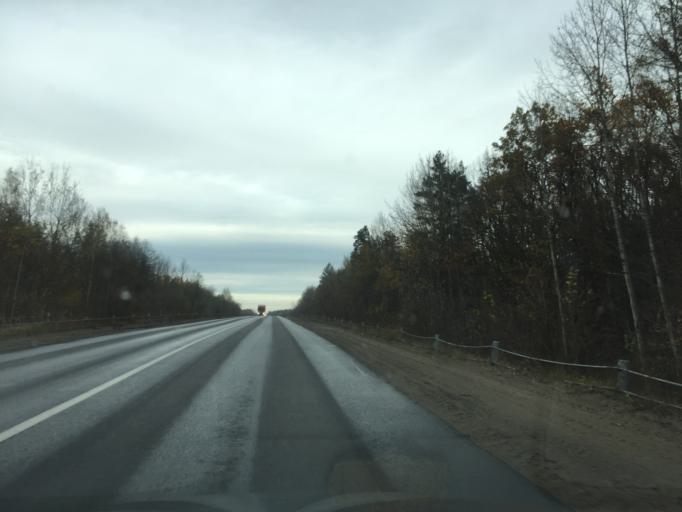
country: BY
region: Gomel
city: Gomel
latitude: 52.4141
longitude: 30.8287
